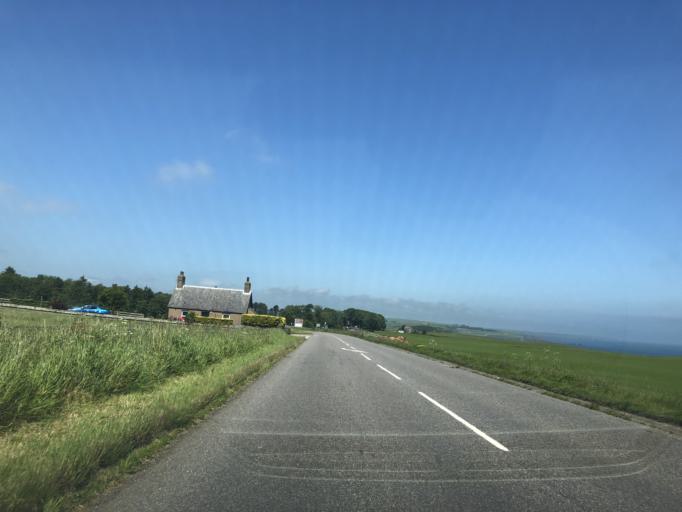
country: GB
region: Scotland
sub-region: Aberdeenshire
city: Stonehaven
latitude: 56.9390
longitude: -2.2070
